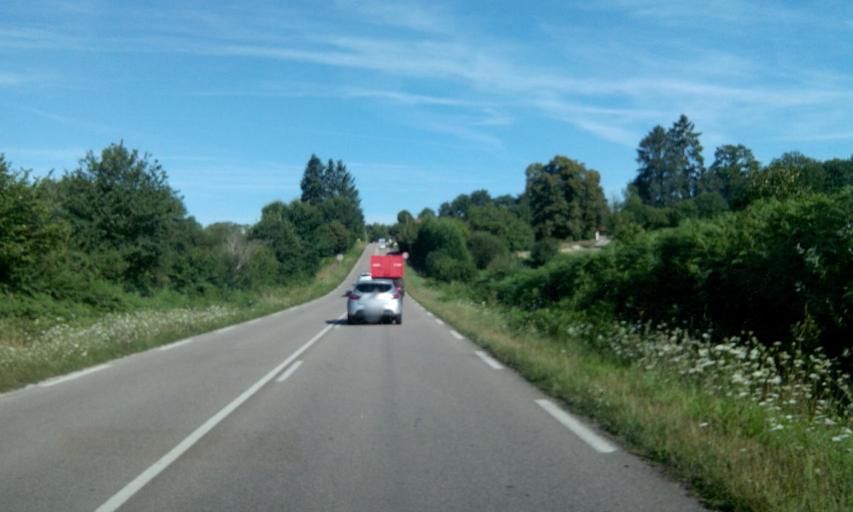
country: FR
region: Limousin
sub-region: Departement de la Haute-Vienne
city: Saint-Leonard-de-Noblat
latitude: 45.8442
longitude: 1.4607
